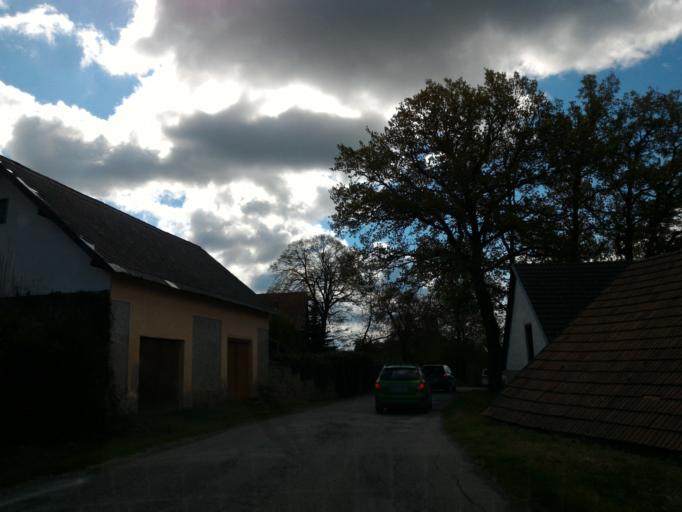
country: CZ
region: Vysocina
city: Ledec nad Sazavou
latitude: 49.6229
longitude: 15.3127
